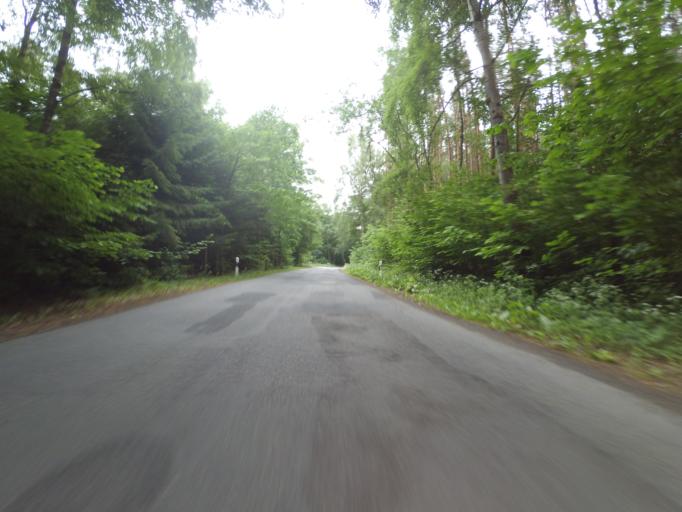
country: DE
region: Mecklenburg-Vorpommern
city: Demen
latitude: 53.6372
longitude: 11.8278
